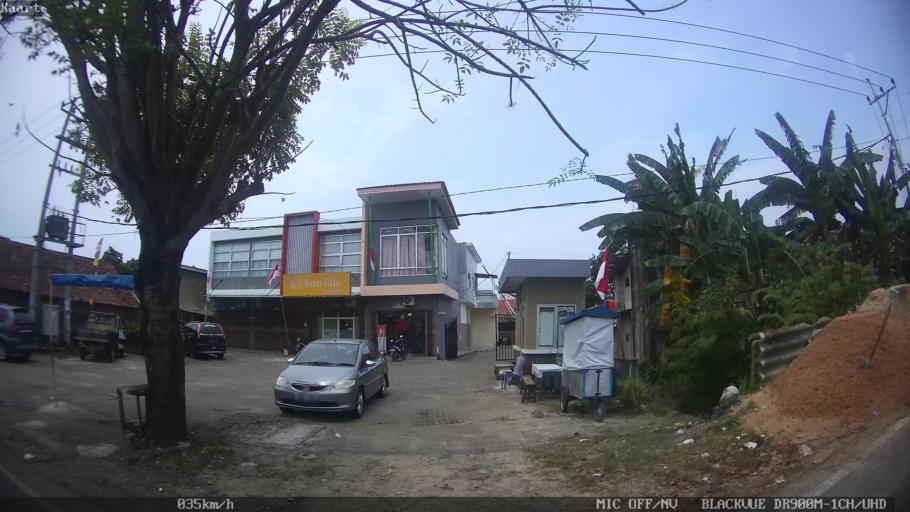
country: ID
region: Lampung
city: Bandarlampung
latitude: -5.4202
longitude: 105.2712
